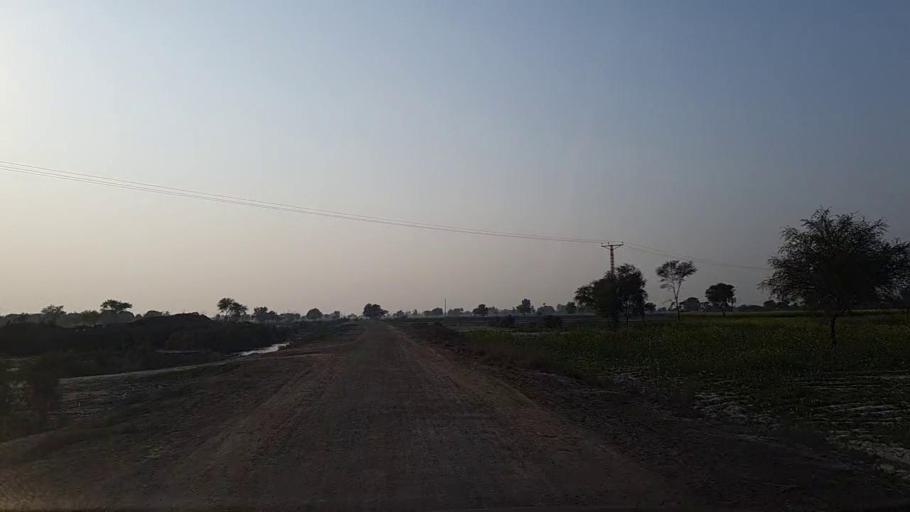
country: PK
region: Sindh
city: Daur
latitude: 26.4071
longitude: 68.3859
